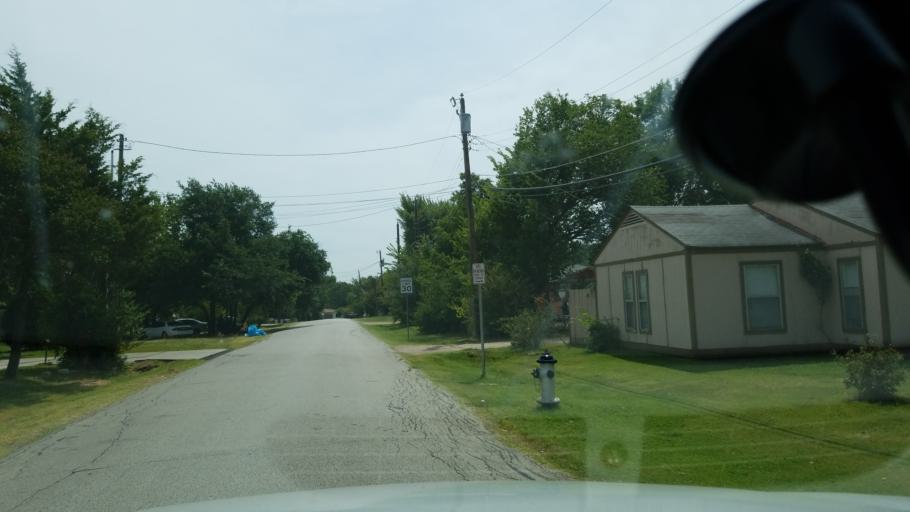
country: US
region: Texas
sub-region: Dallas County
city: Irving
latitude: 32.8312
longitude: -96.9921
